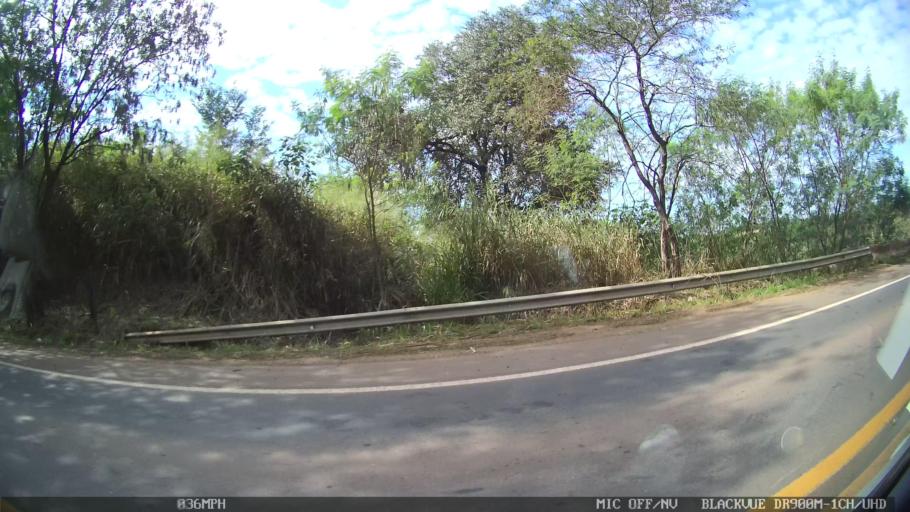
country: BR
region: Sao Paulo
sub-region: Santa Barbara D'Oeste
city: Santa Barbara d'Oeste
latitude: -22.7105
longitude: -47.4284
